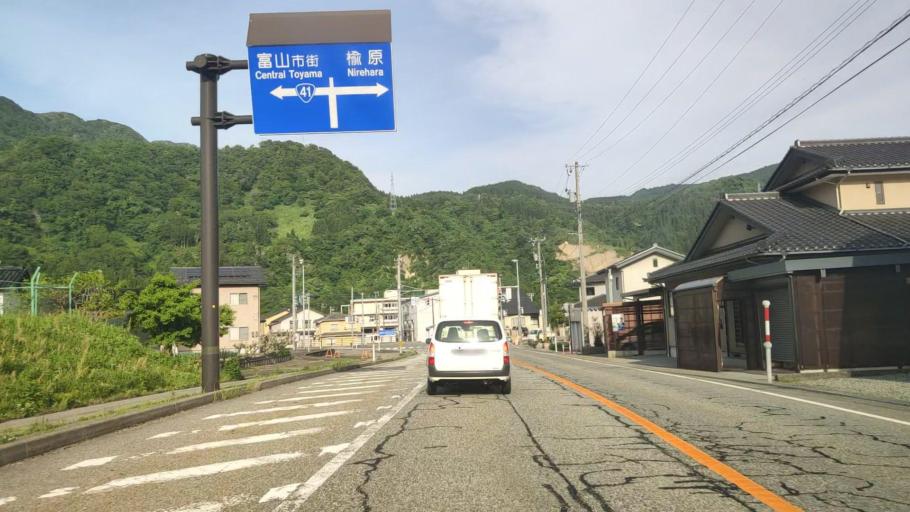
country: JP
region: Toyama
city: Yatsuomachi-higashikumisaka
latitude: 36.5360
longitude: 137.2301
